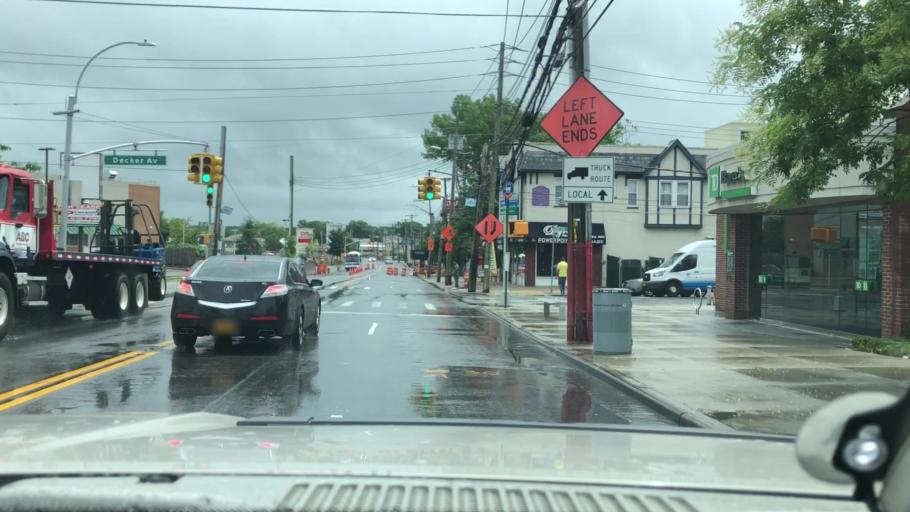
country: US
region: New York
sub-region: Richmond County
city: Bloomfield
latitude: 40.6246
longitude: -74.1417
